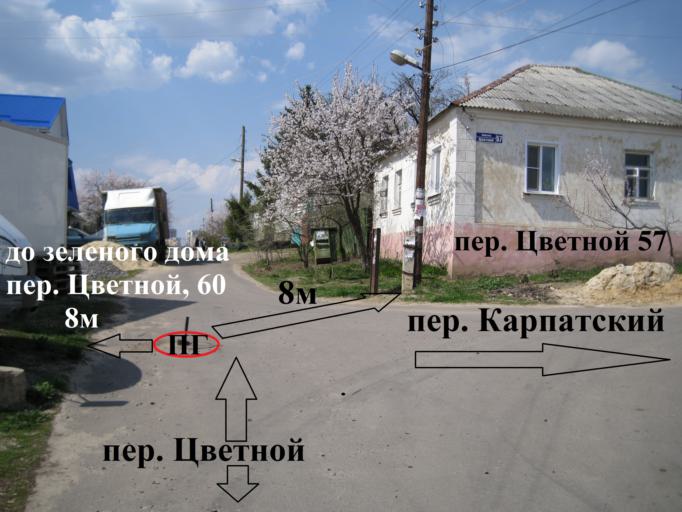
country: RU
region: Voronezj
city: Voronezh
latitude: 51.6410
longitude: 39.1975
